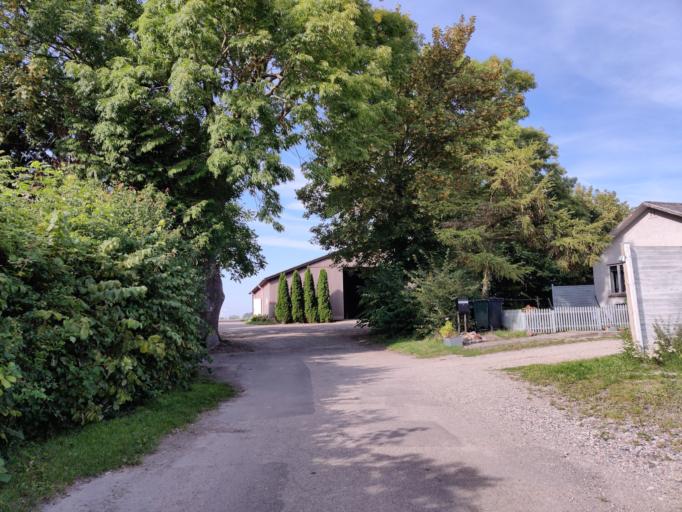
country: DK
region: Zealand
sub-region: Guldborgsund Kommune
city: Nykobing Falster
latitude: 54.6542
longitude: 11.8935
